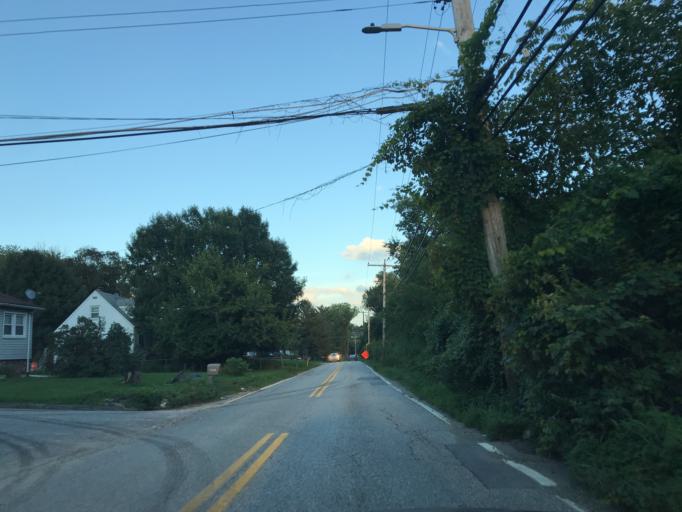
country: US
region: Maryland
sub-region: Baltimore County
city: Woodlawn
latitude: 39.3182
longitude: -76.7336
